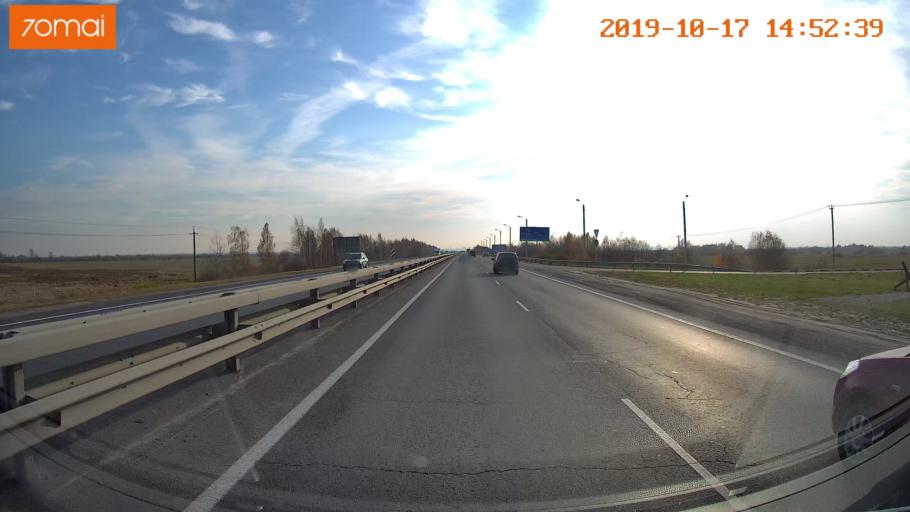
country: RU
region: Rjazan
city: Polyany
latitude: 54.7047
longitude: 39.8442
